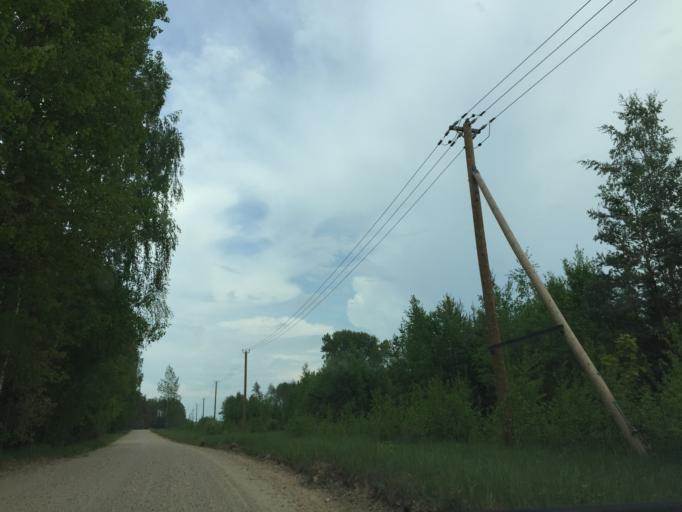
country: LV
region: Livani
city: Livani
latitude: 56.5570
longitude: 26.1134
